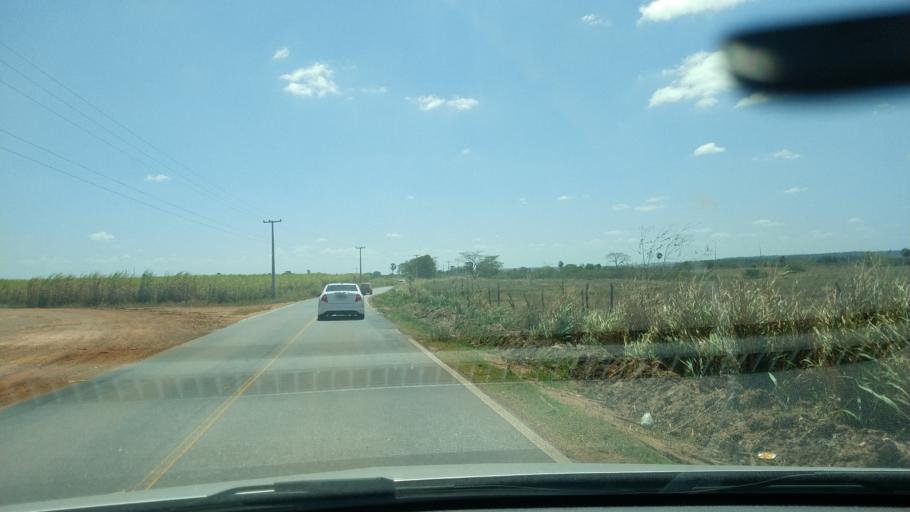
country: BR
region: Rio Grande do Norte
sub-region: Goianinha
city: Goianinha
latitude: -6.2531
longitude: -35.1890
